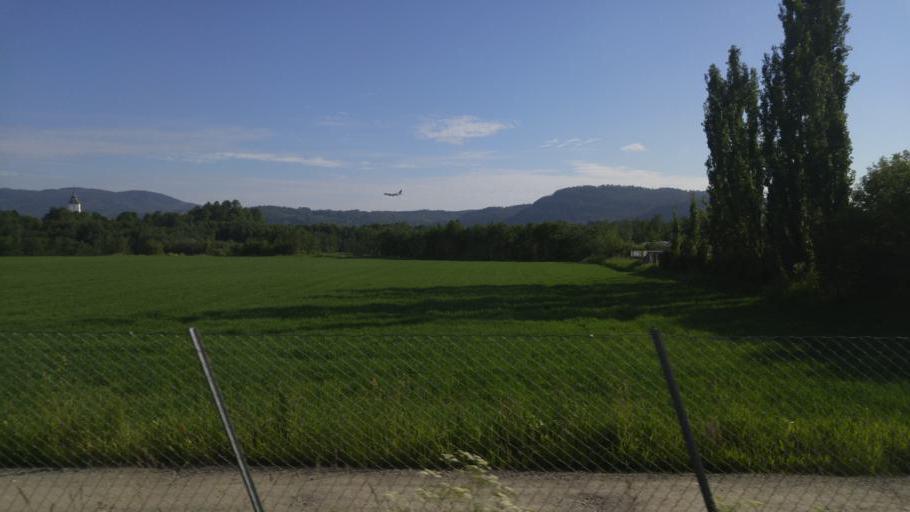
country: NO
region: Nord-Trondelag
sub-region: Stjordal
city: Stjordalshalsen
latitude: 63.4475
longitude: 10.9562
